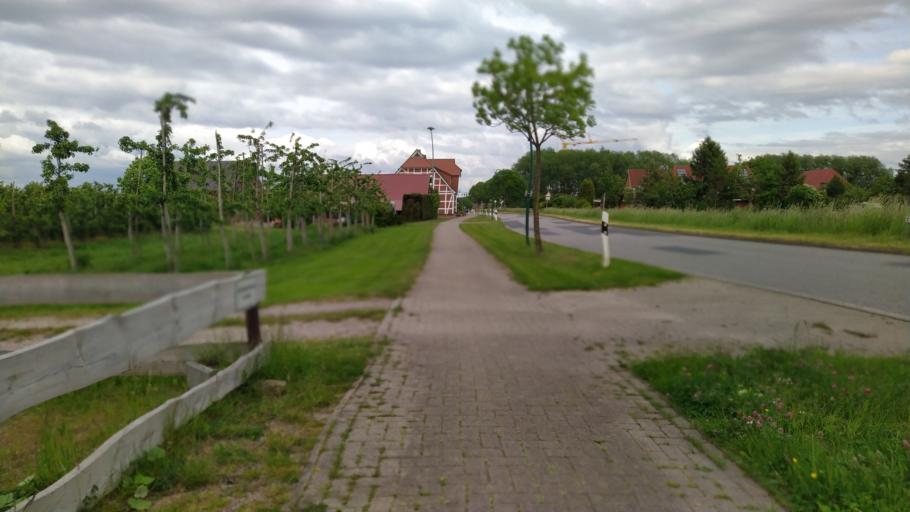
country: DE
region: Lower Saxony
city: Neu Wulmstorf
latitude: 53.4907
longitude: 9.7542
